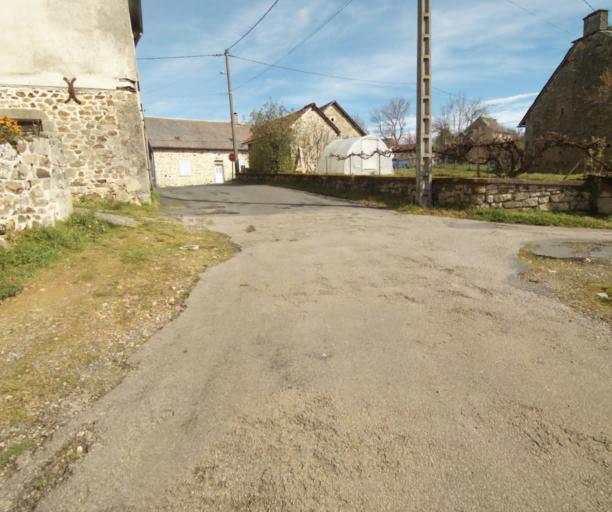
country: FR
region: Limousin
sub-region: Departement de la Correze
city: Laguenne
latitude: 45.2727
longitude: 1.8202
